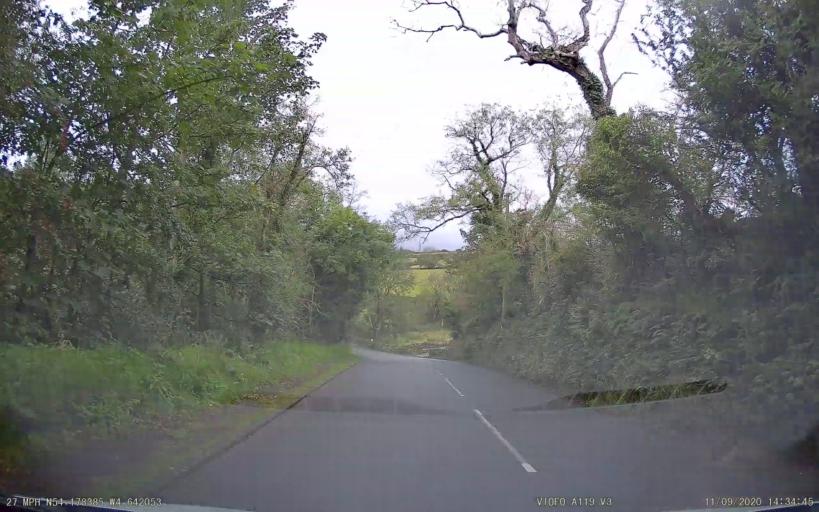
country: IM
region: Castletown
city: Castletown
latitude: 54.1784
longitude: -4.6421
